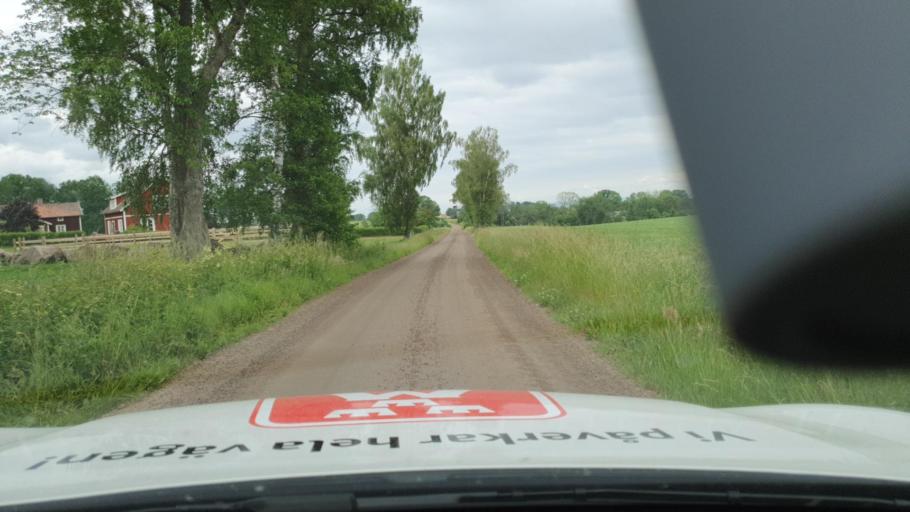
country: SE
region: Vaestra Goetaland
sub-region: Hjo Kommun
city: Hjo
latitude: 58.2069
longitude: 14.1777
